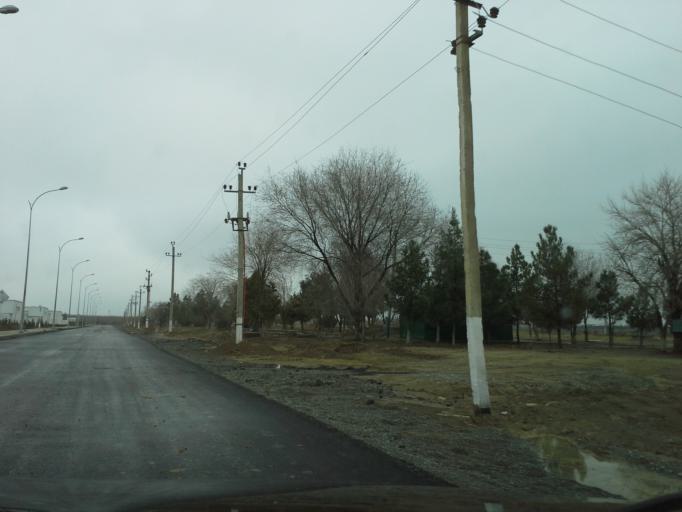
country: TM
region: Ahal
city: Ashgabat
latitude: 37.9730
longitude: 58.4031
